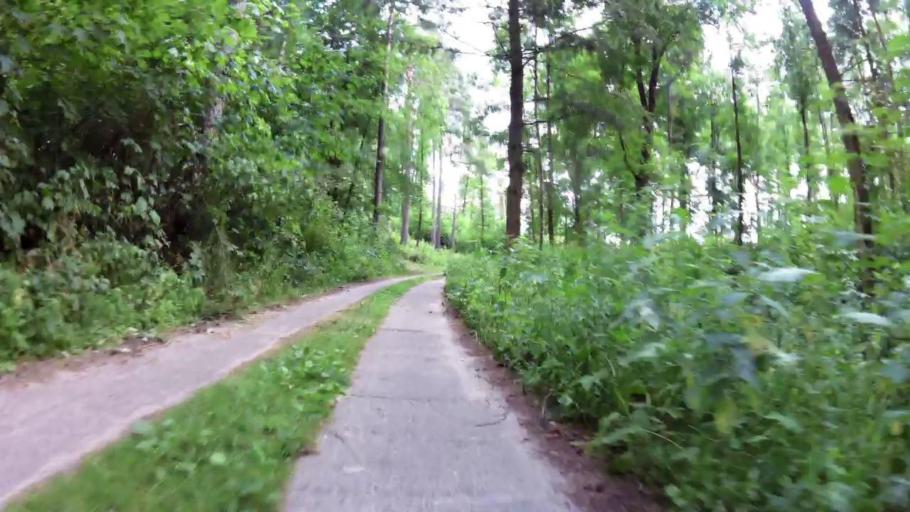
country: PL
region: West Pomeranian Voivodeship
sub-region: Powiat lobeski
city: Lobez
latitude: 53.6508
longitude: 15.5795
